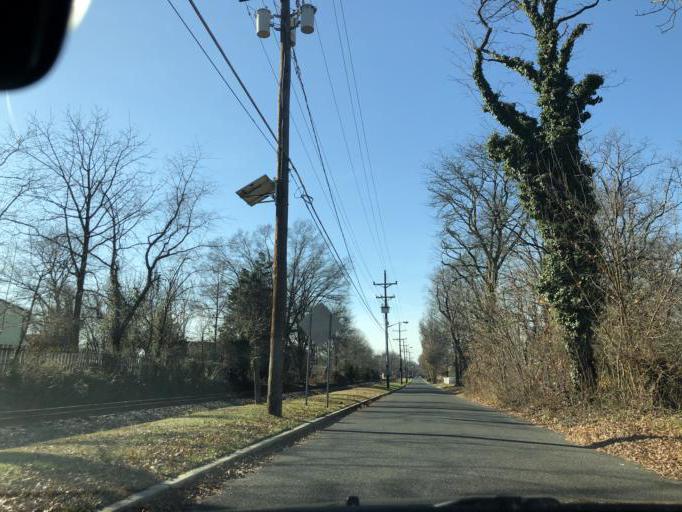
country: US
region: New Jersey
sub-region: Burlington County
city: Moorestown-Lenola
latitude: 39.9619
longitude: -74.9771
